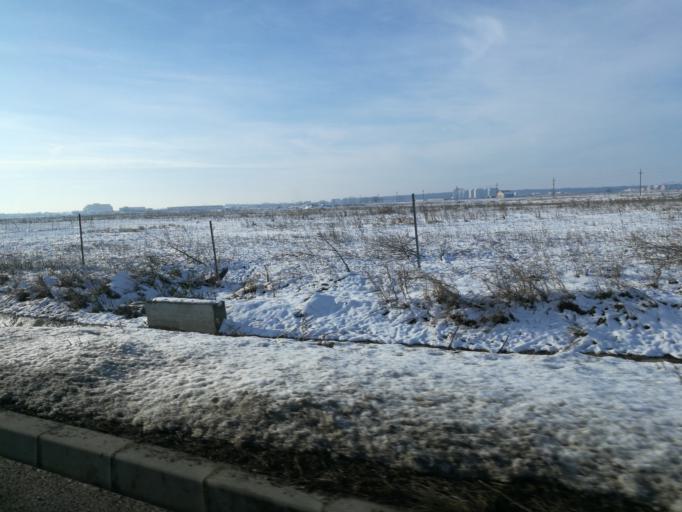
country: RO
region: Ilfov
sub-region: Voluntari City
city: Voluntari
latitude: 44.5178
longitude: 26.1695
